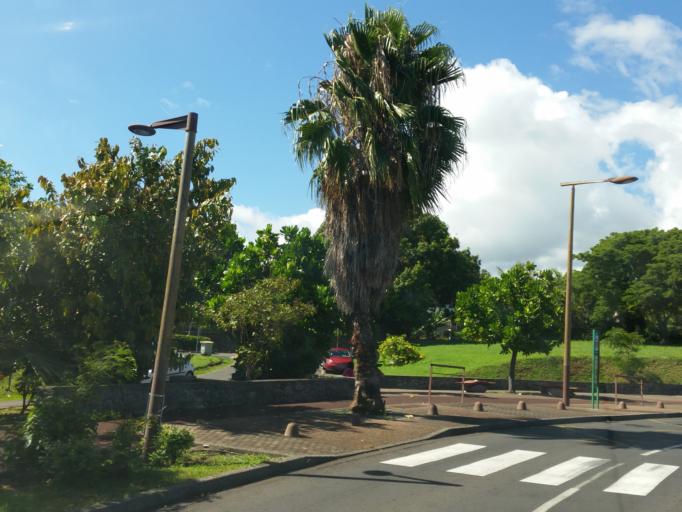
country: RE
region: Reunion
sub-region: Reunion
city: Sainte-Marie
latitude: -20.8961
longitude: 55.5445
